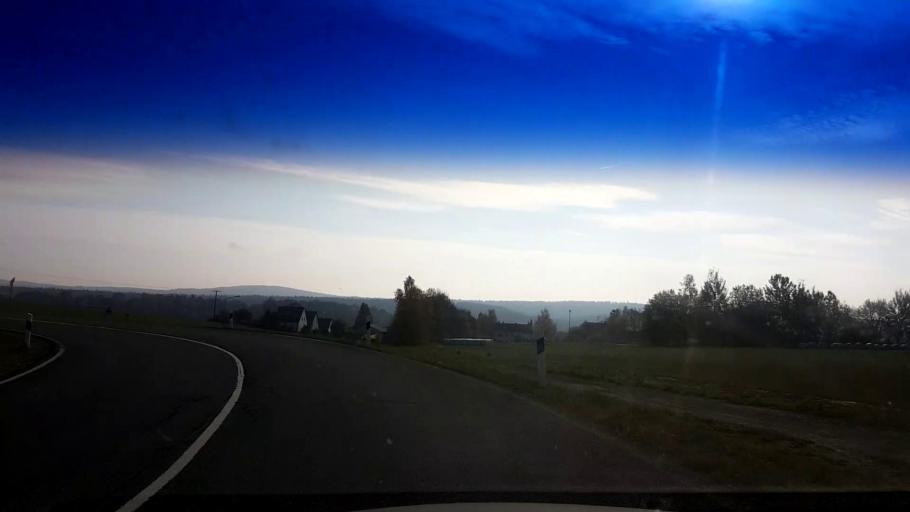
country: DE
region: Bavaria
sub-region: Upper Franconia
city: Schirnding
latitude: 50.0858
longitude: 12.2218
